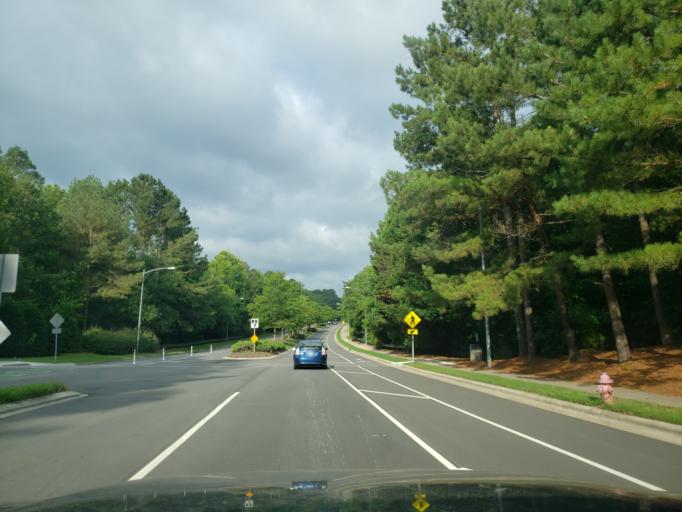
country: US
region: North Carolina
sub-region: Durham County
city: Durham
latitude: 35.9299
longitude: -78.9435
